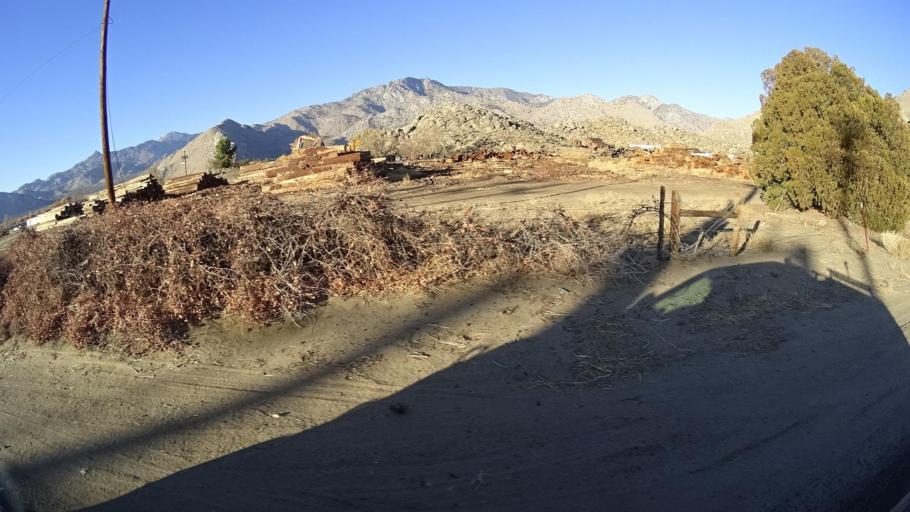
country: US
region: California
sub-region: Kern County
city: Weldon
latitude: 35.6670
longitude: -118.2622
